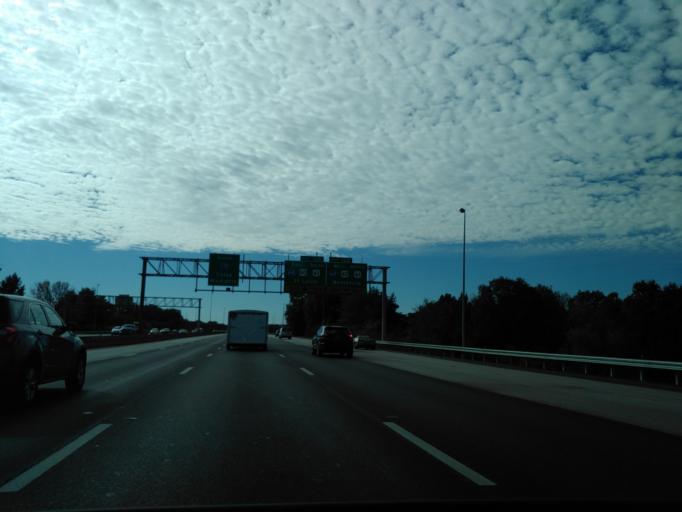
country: US
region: Missouri
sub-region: Saint Louis County
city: Creve Coeur
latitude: 38.6472
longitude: -90.4489
